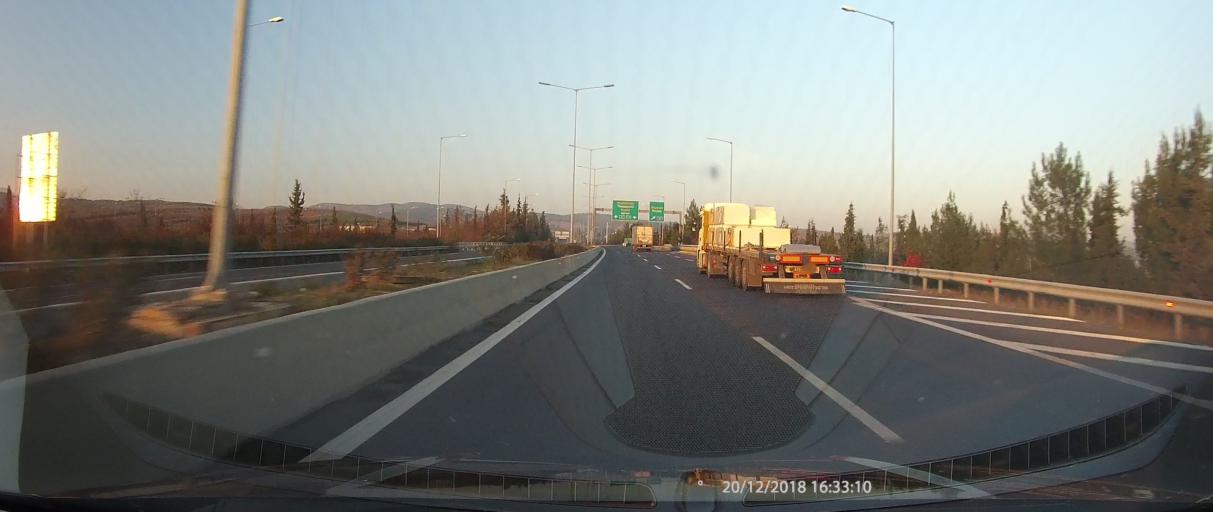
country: GR
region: Thessaly
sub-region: Nomos Magnisias
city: Evxinoupolis
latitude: 39.2589
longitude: 22.7365
